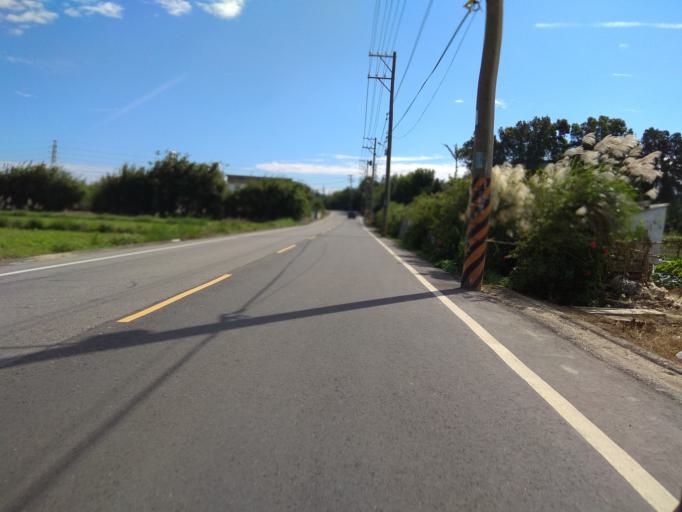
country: TW
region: Taiwan
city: Taoyuan City
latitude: 25.0415
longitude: 121.1243
